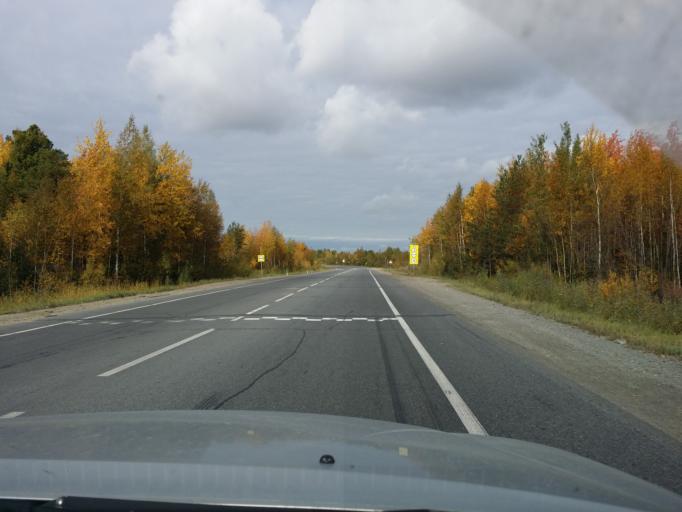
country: RU
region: Khanty-Mansiyskiy Avtonomnyy Okrug
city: Megion
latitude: 61.1082
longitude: 76.0392
